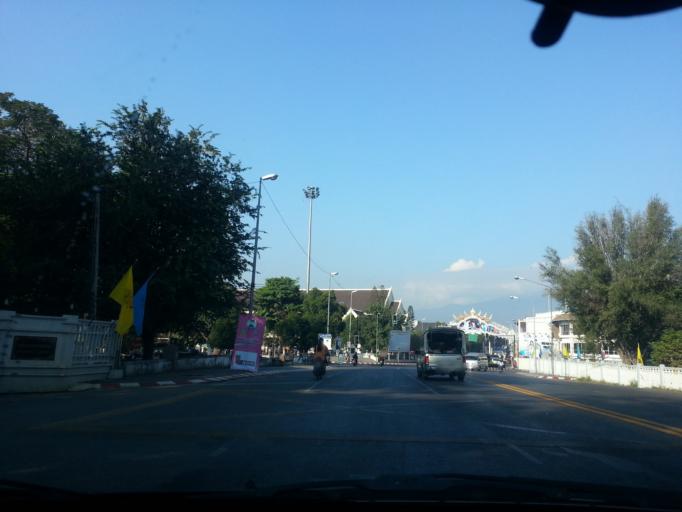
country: TH
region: Chiang Mai
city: Chiang Mai
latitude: 18.7875
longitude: 99.0034
